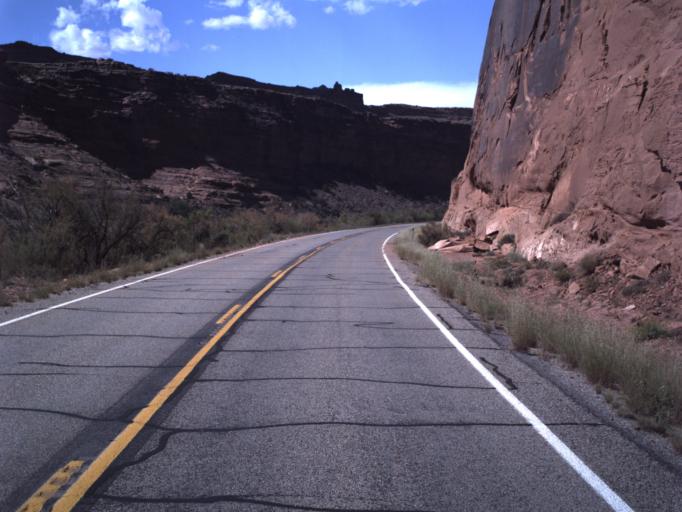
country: US
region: Utah
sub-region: Grand County
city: Moab
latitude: 38.5343
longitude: -109.6257
